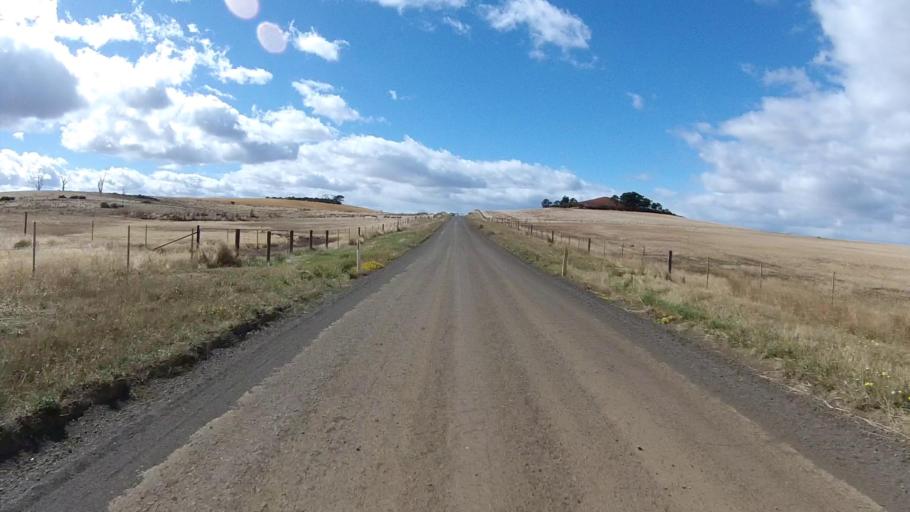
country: AU
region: Tasmania
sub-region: Northern Midlands
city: Evandale
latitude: -41.7144
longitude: 147.4157
